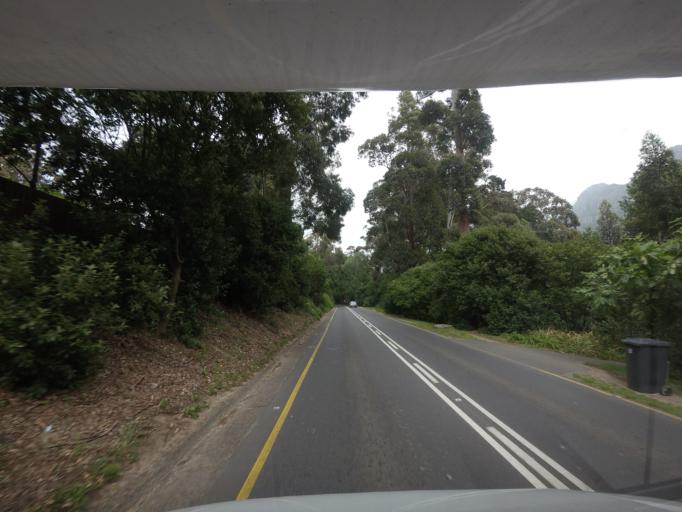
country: ZA
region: Western Cape
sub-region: City of Cape Town
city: Constantia
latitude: -34.0143
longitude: 18.3867
